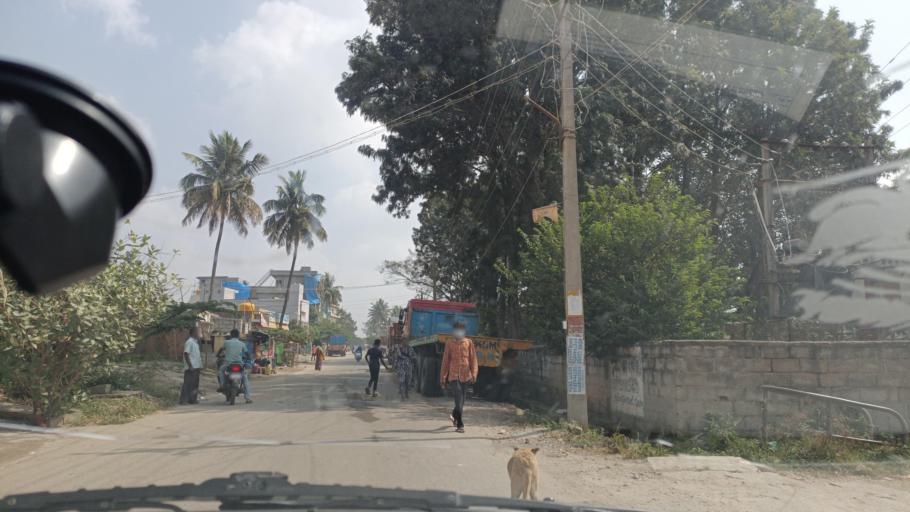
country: IN
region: Karnataka
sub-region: Bangalore Urban
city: Yelahanka
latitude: 13.1563
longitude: 77.6182
